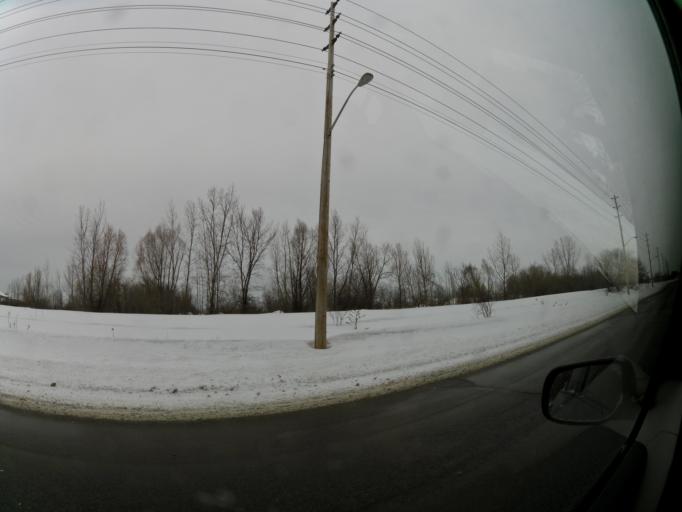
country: CA
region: Ontario
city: Ottawa
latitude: 45.3752
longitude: -75.6184
